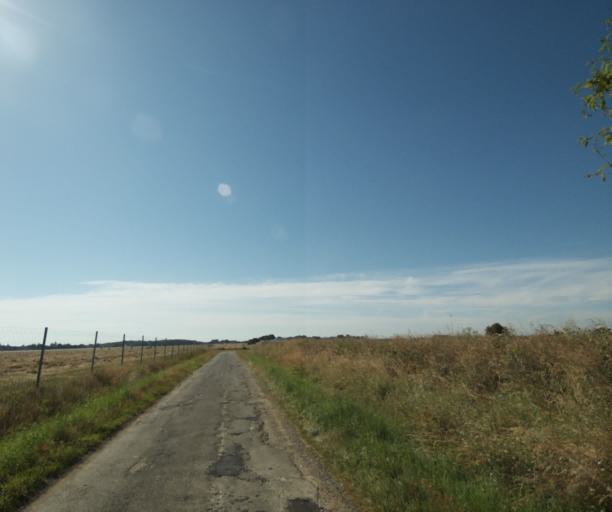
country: FR
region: Pays de la Loire
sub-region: Departement de la Mayenne
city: Laval
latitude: 48.0321
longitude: -0.7466
